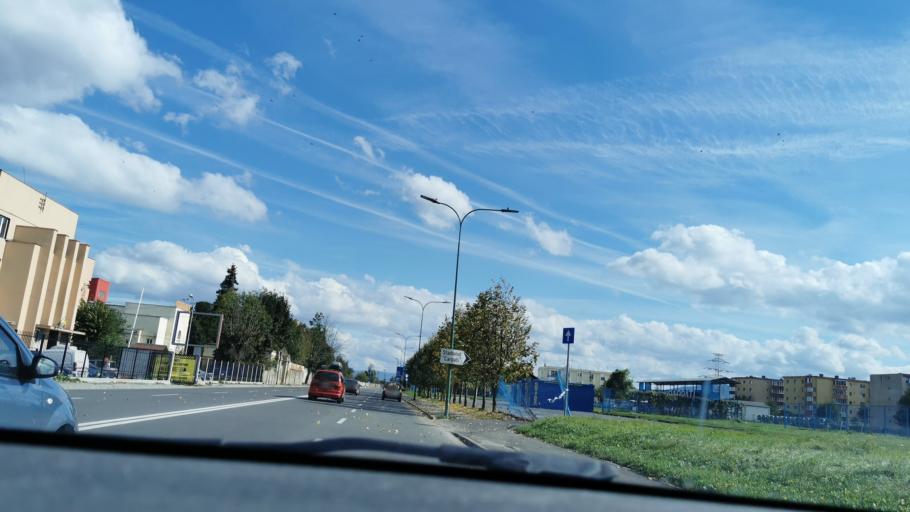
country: RO
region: Brasov
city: Brasov
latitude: 45.6493
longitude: 25.6494
